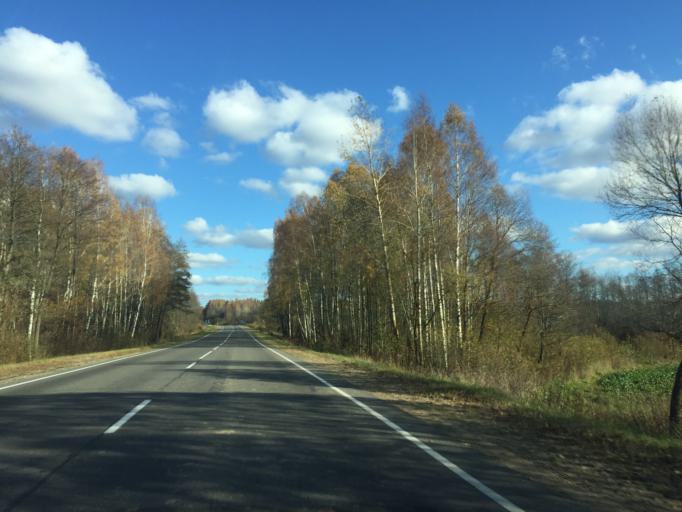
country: BY
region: Vitebsk
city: Pastavy
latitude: 55.0043
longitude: 26.8440
